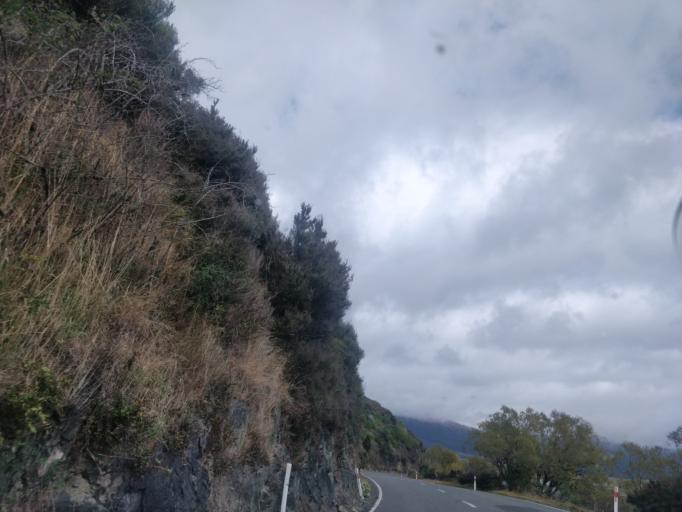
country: NZ
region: Canterbury
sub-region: Waimakariri District
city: Oxford
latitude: -43.0137
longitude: 171.7137
